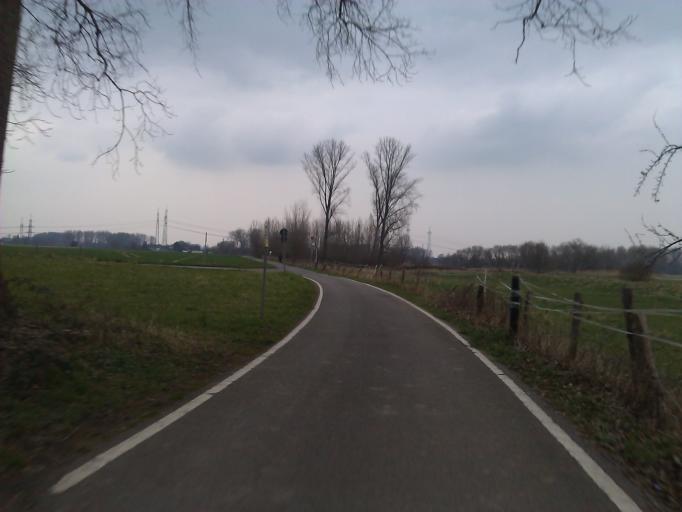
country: DE
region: North Rhine-Westphalia
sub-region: Regierungsbezirk Koln
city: Leverkusen
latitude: 51.0322
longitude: 6.9552
